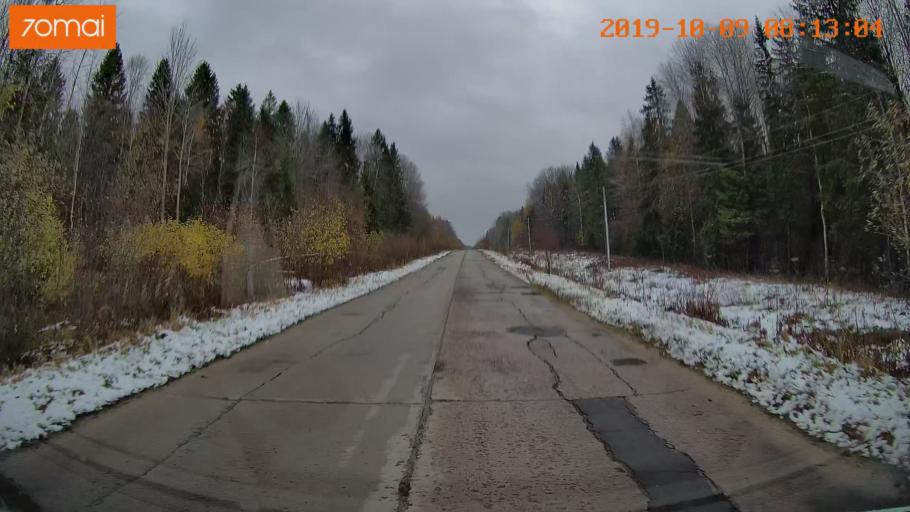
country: RU
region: Vologda
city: Gryazovets
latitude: 58.7217
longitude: 40.1343
